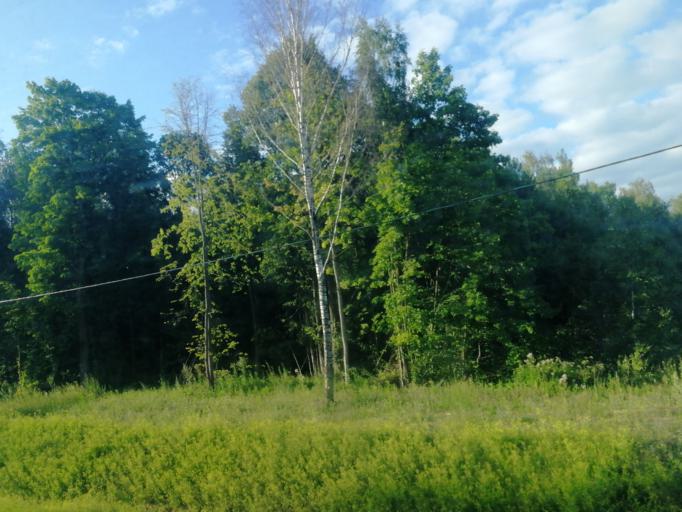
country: RU
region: Kaluga
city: Kaluga
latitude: 54.4399
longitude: 36.3327
